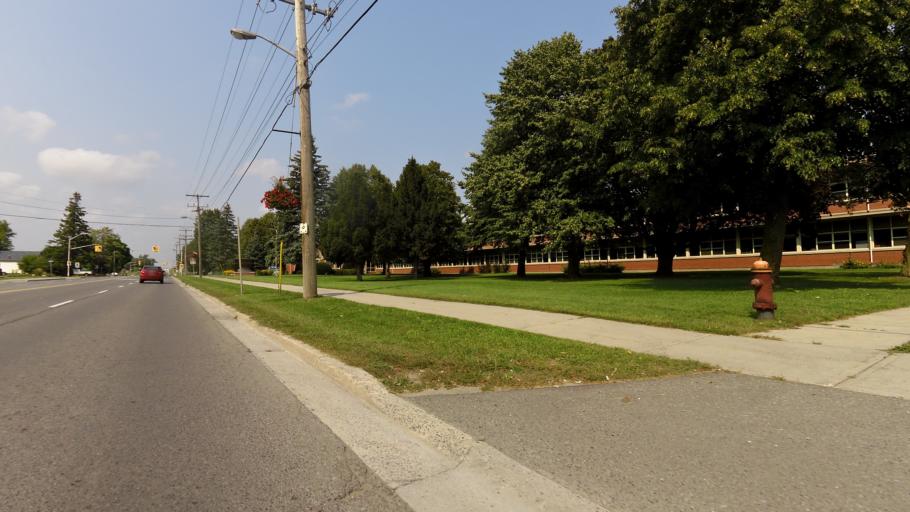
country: CA
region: Ontario
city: Prescott
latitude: 44.7189
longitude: -75.5218
